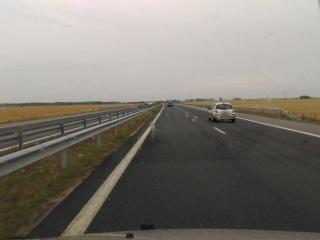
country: BG
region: Stara Zagora
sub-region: Obshtina Radnevo
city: Radnevo
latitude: 42.3698
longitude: 25.8009
